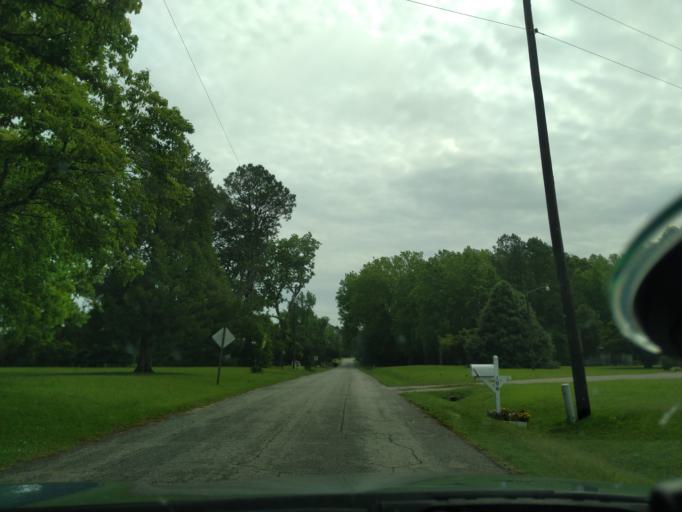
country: US
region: North Carolina
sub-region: Chowan County
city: Edenton
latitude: 35.9316
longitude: -76.6141
